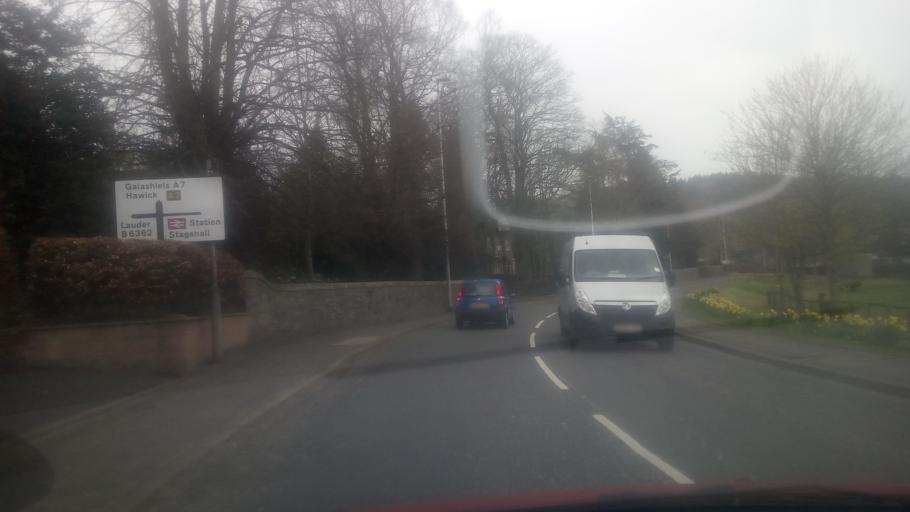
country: GB
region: Scotland
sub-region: The Scottish Borders
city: Galashiels
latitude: 55.6936
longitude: -2.8618
